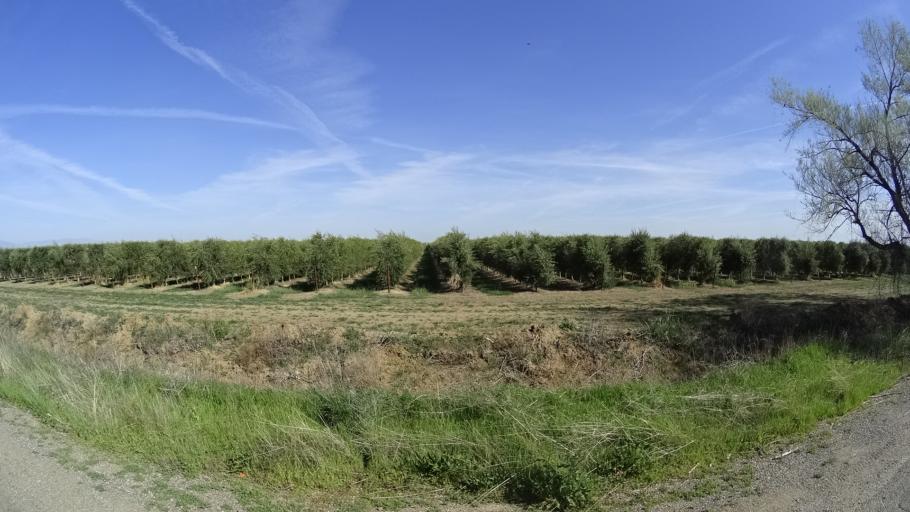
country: US
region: California
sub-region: Glenn County
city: Willows
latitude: 39.6115
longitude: -122.2433
